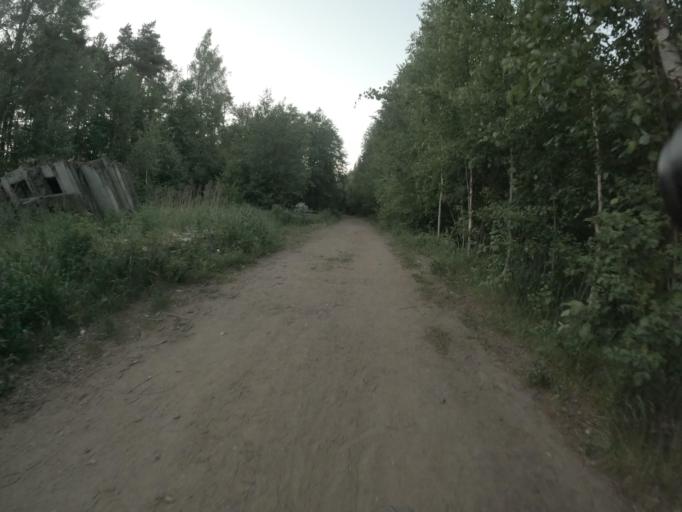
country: RU
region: St.-Petersburg
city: Krasnogvargeisky
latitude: 59.9872
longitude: 30.5309
